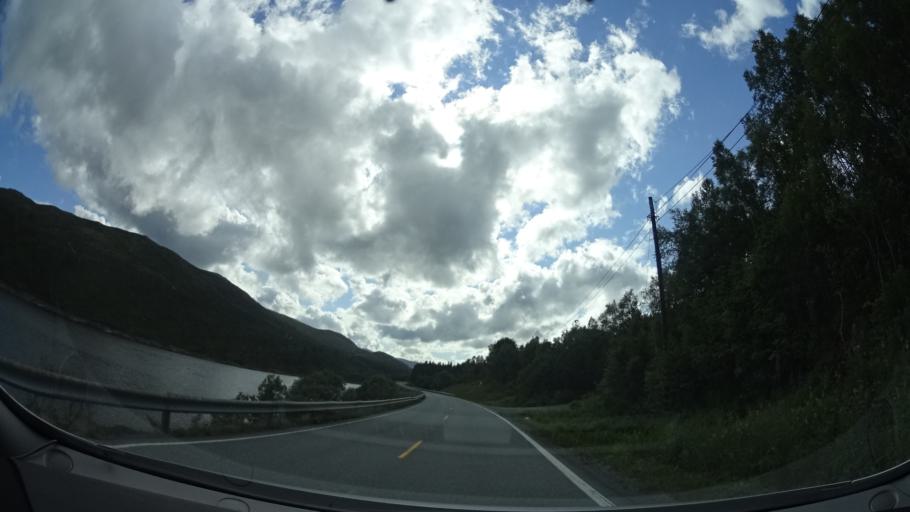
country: NO
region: More og Romsdal
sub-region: Rindal
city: Rindal
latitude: 63.2238
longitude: 9.2505
